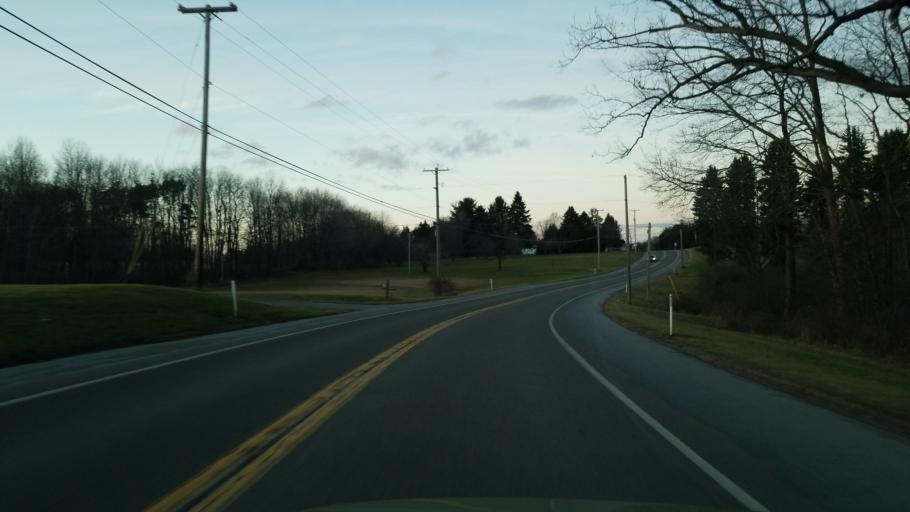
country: US
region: Pennsylvania
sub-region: Jefferson County
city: Punxsutawney
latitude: 40.8864
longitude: -79.0172
